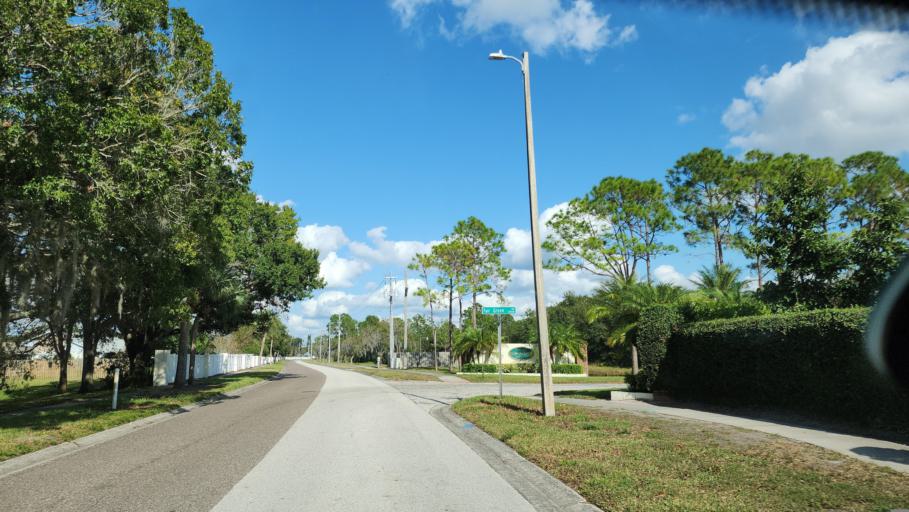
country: US
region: Florida
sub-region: Hillsborough County
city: Riverview
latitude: 27.7995
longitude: -82.3163
